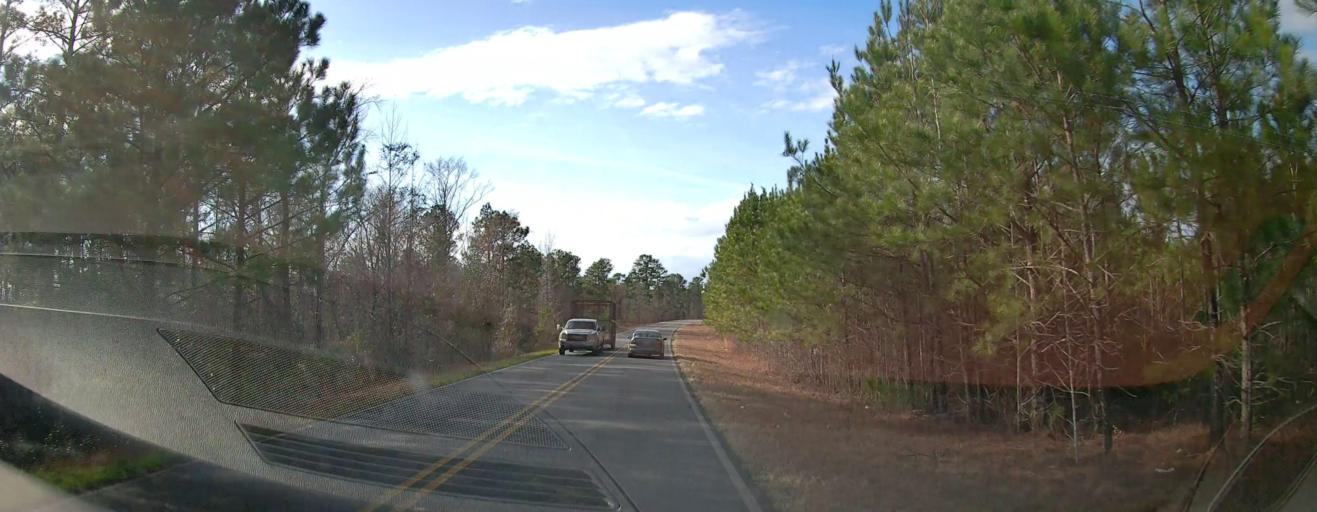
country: US
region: Georgia
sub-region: Talbot County
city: Talbotton
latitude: 32.5161
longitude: -84.5992
